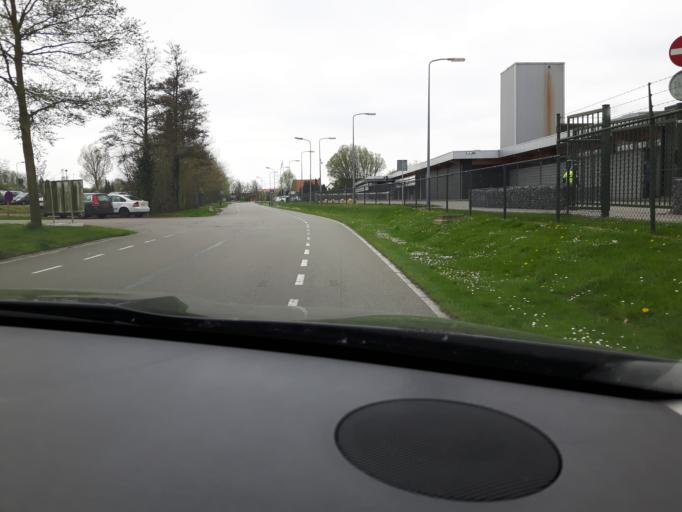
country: NL
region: Zeeland
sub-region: Gemeente Reimerswaal
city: Yerseke
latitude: 51.4734
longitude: 3.9703
